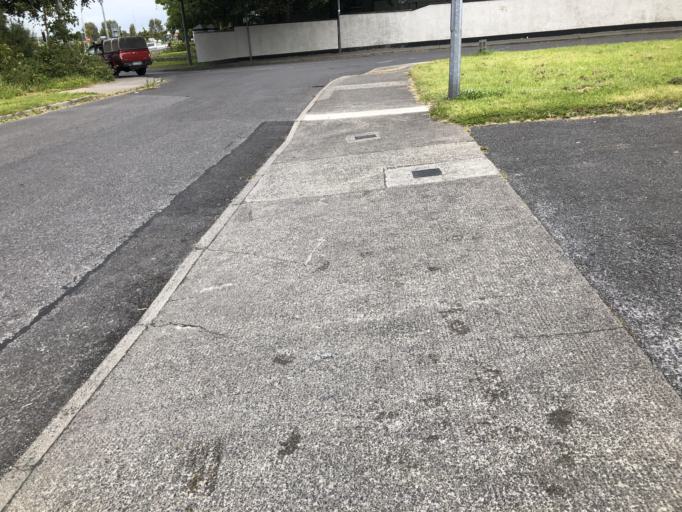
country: IE
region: Connaught
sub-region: County Galway
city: Gaillimh
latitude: 53.2736
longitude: -9.0812
